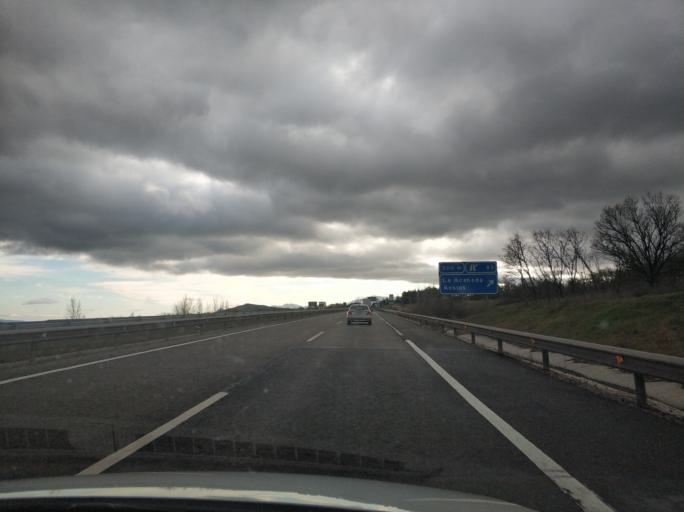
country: ES
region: Madrid
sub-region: Provincia de Madrid
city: Horcajo de la Sierra
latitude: 41.0716
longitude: -3.6057
